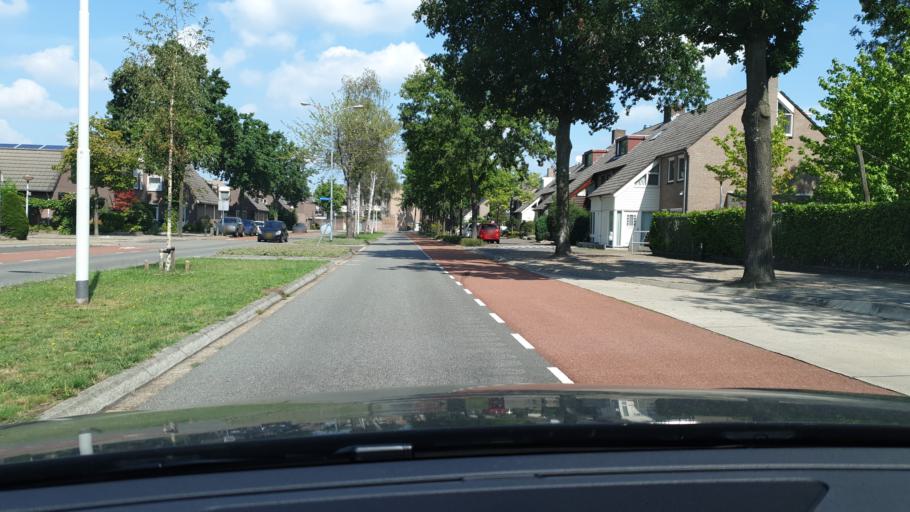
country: NL
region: North Brabant
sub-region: Gemeente Eindhoven
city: Eindhoven
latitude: 51.4807
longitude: 5.4501
